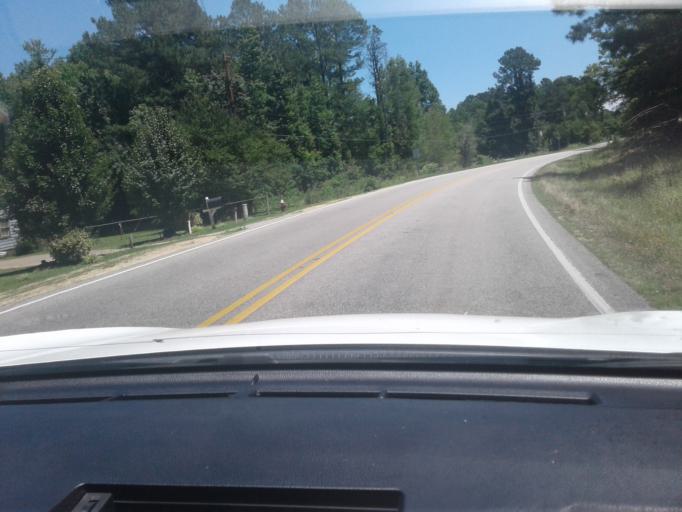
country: US
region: North Carolina
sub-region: Harnett County
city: Erwin
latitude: 35.3176
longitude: -78.7085
